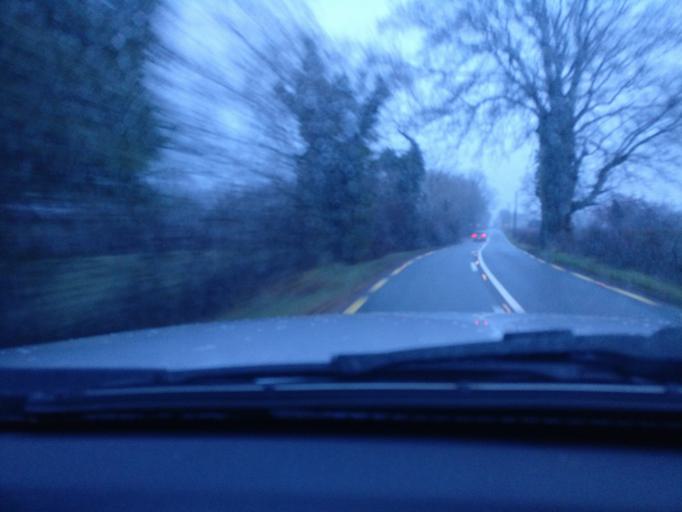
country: IE
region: Leinster
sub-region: An Mhi
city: Athboy
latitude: 53.6400
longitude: -6.8338
